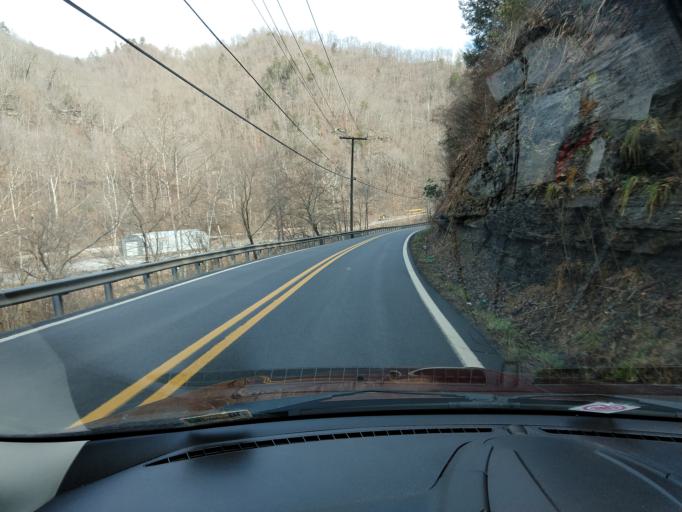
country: US
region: West Virginia
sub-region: McDowell County
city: Welch
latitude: 37.3415
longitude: -81.7389
